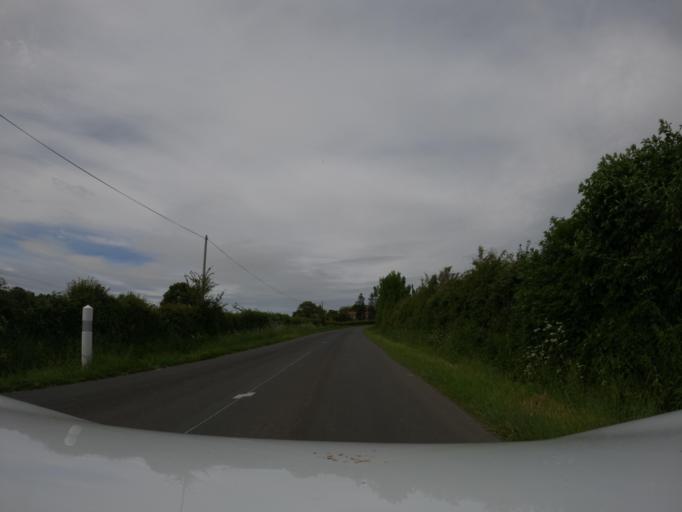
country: FR
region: Pays de la Loire
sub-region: Departement de la Vendee
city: Foussais-Payre
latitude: 46.5144
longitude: -0.6506
